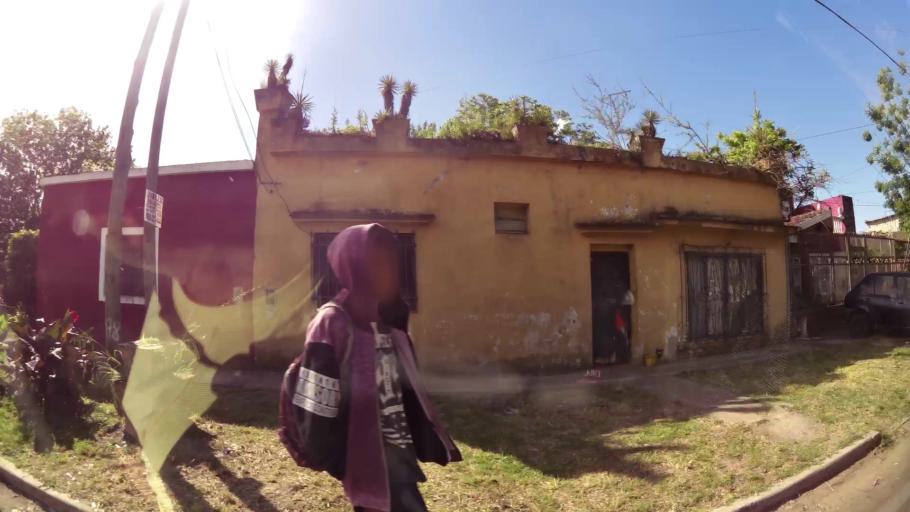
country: AR
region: Buenos Aires
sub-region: Partido de Almirante Brown
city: Adrogue
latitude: -34.8037
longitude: -58.3623
